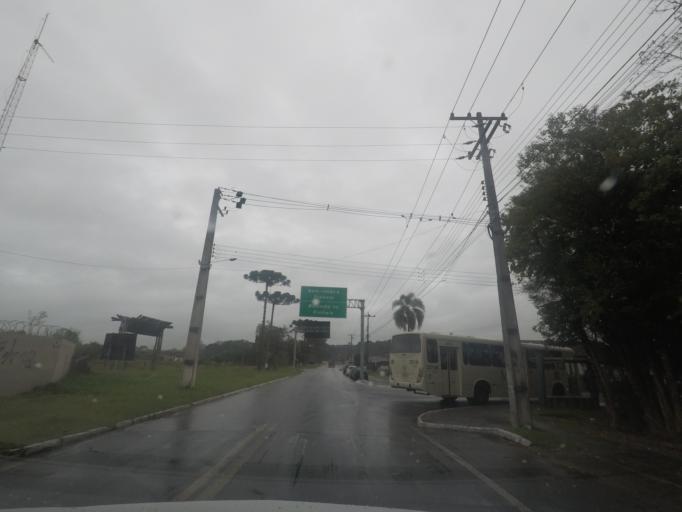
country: BR
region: Parana
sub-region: Quatro Barras
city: Quatro Barras
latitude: -25.3782
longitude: -49.1203
